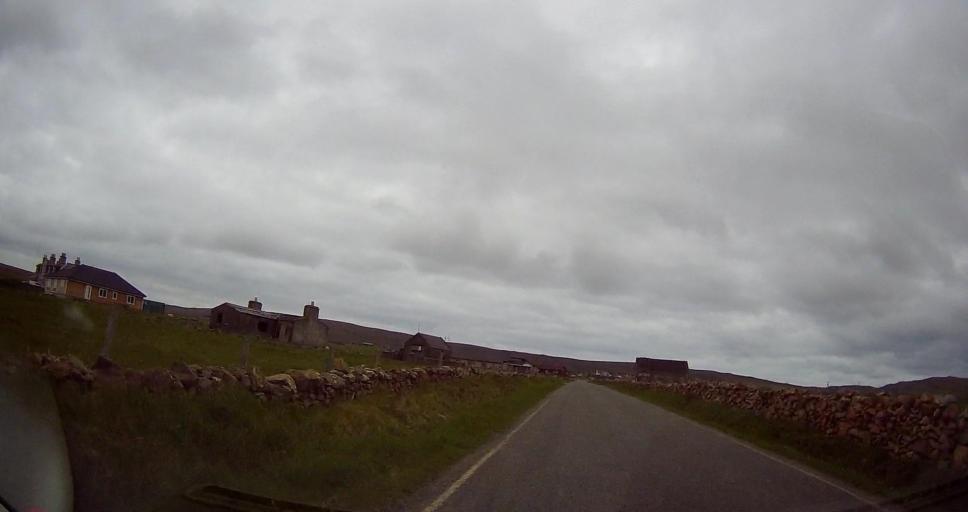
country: GB
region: Scotland
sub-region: Shetland Islands
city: Shetland
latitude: 60.7574
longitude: -0.8702
